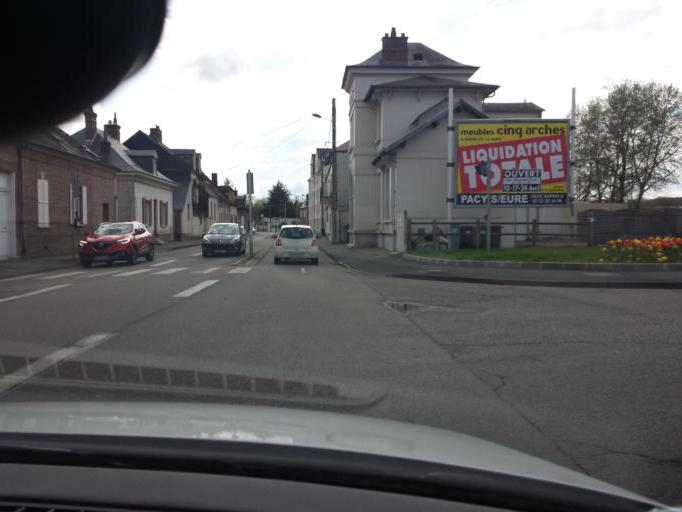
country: FR
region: Haute-Normandie
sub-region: Departement de l'Eure
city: Evreux
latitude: 49.0209
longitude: 1.1348
